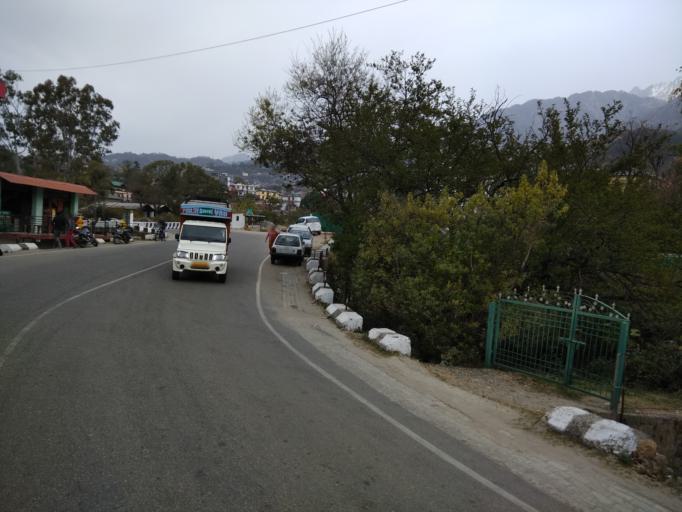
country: IN
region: Himachal Pradesh
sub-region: Kangra
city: Dharmsala
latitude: 32.2050
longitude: 76.3291
